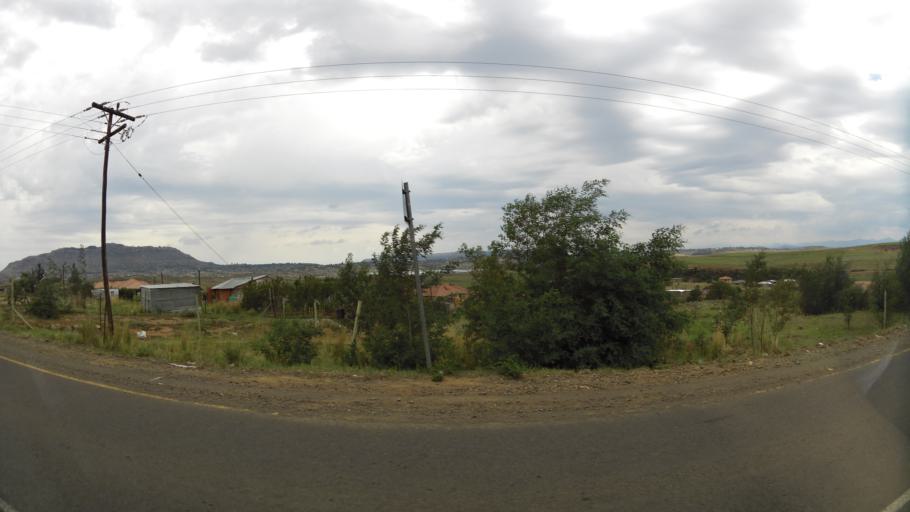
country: LS
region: Maseru
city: Maseru
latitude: -29.3924
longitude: 27.4735
